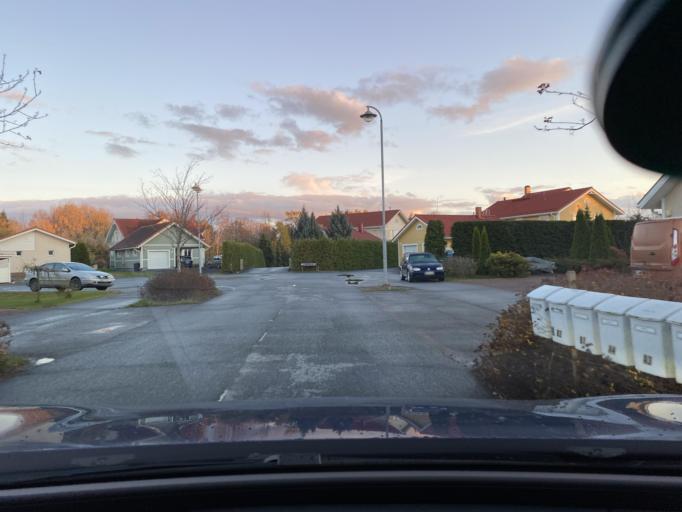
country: FI
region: Satakunta
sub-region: Pori
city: Huittinen
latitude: 61.1807
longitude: 22.7050
